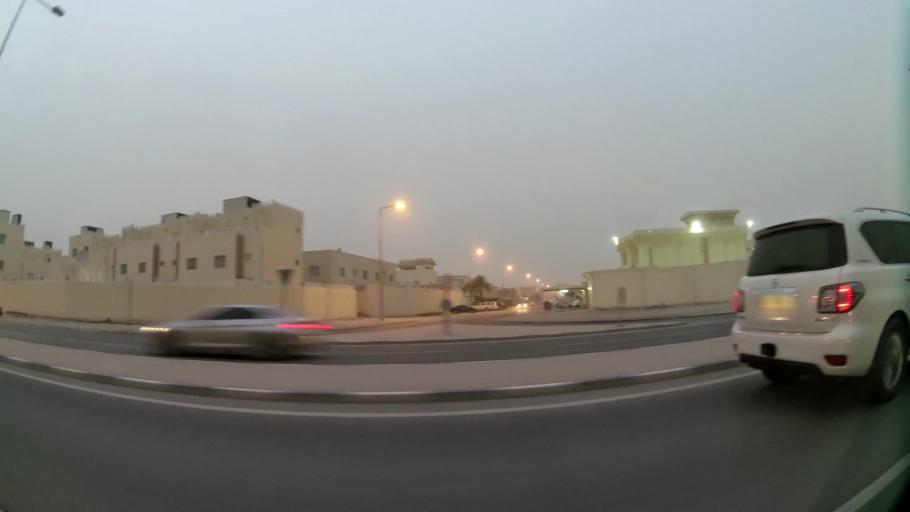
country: QA
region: Baladiyat ad Dawhah
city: Doha
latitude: 25.2327
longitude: 51.4920
